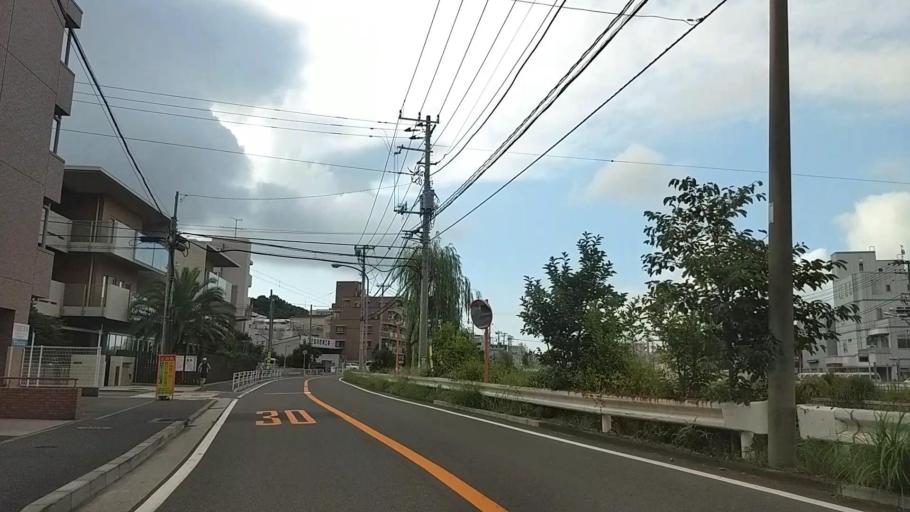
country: JP
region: Kanagawa
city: Yokohama
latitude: 35.4285
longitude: 139.6222
